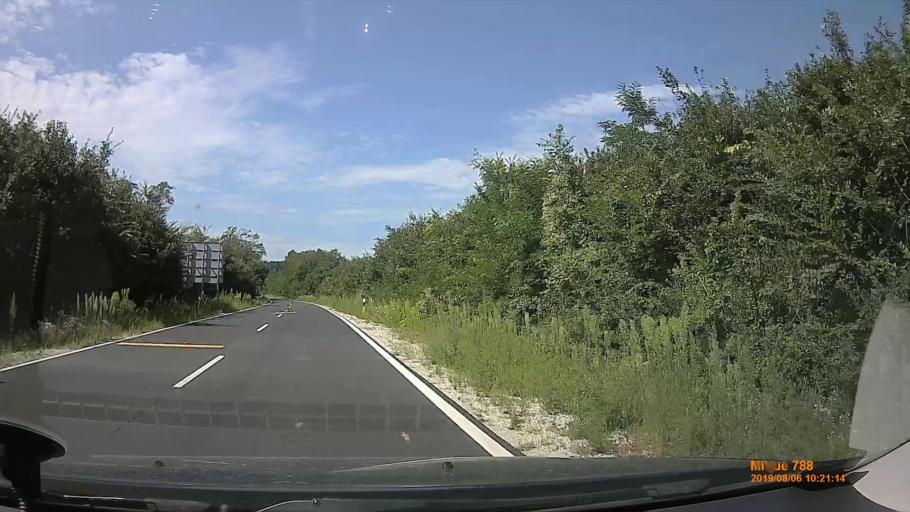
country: HU
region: Somogy
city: Balatonbereny
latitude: 46.6774
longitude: 17.3362
